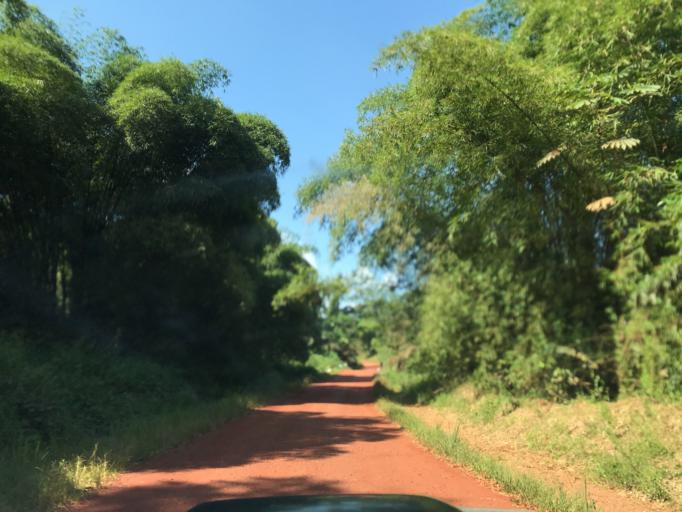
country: CD
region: Eastern Province
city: Kisangani
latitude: 1.2049
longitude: 25.2591
